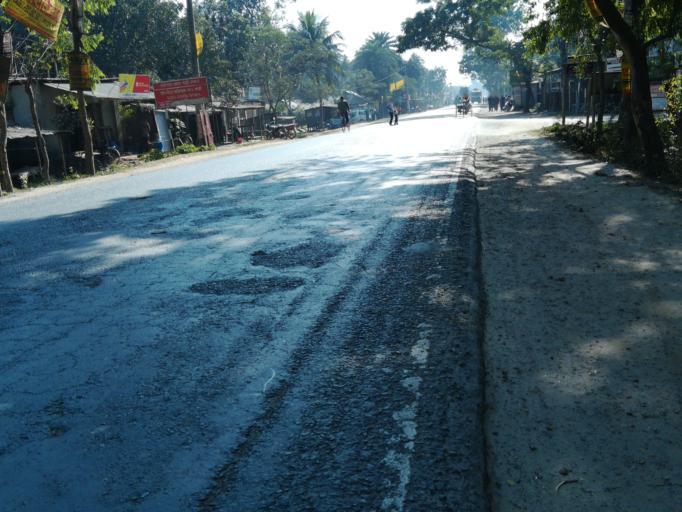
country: BD
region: Rangpur Division
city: Rangpur
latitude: 25.5745
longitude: 89.2745
